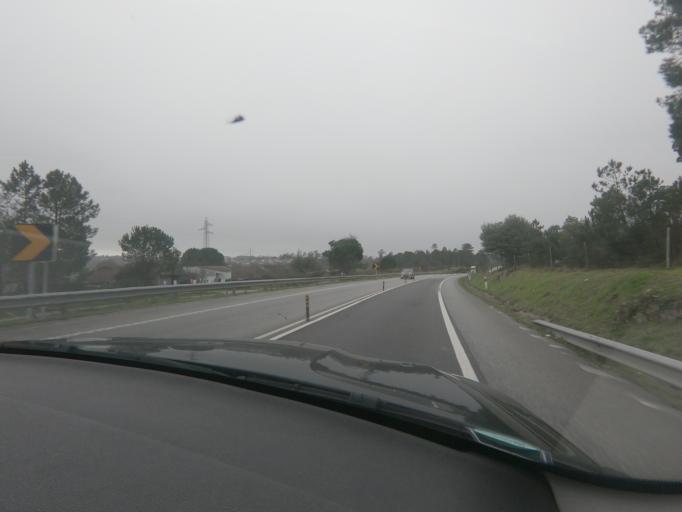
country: PT
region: Viseu
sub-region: Concelho de Tondela
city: Tondela
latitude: 40.5286
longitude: -8.0698
